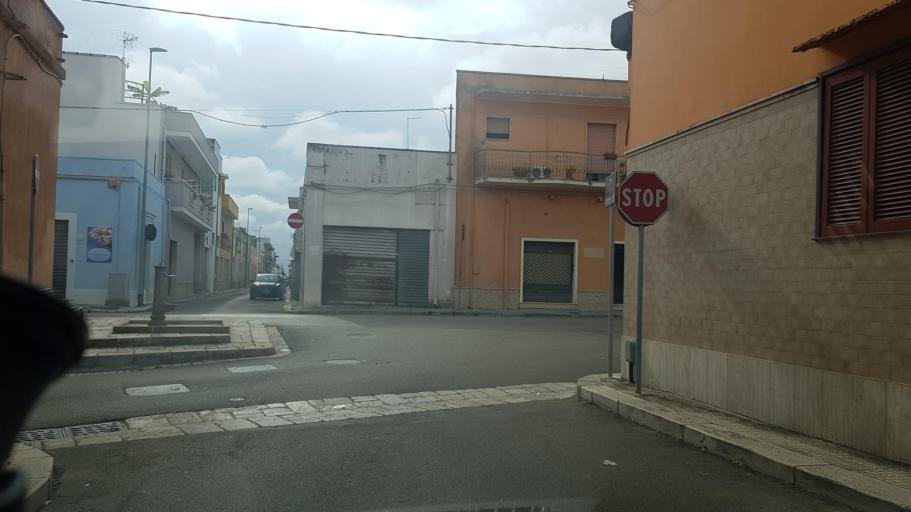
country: IT
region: Apulia
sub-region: Provincia di Lecce
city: Guagnano
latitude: 40.4012
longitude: 17.9482
